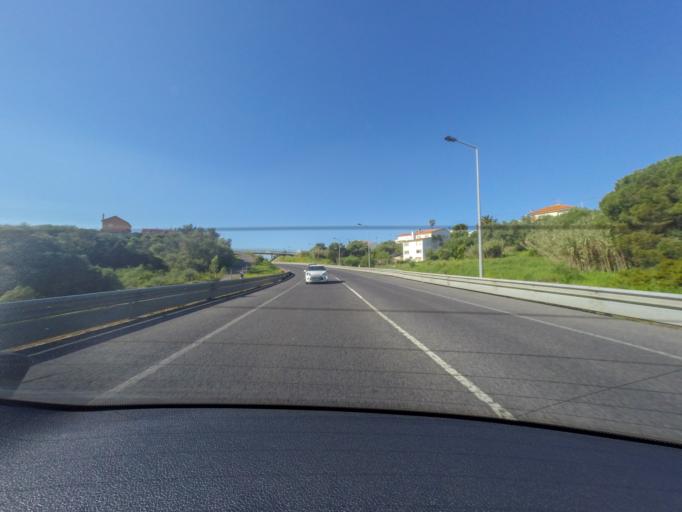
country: PT
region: Lisbon
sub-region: Cascais
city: Alcabideche
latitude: 38.7198
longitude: -9.4169
